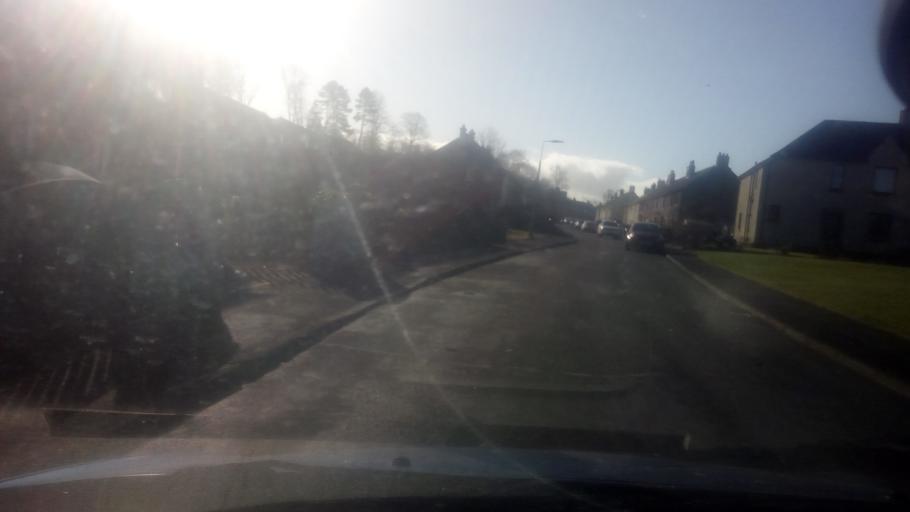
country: GB
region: Scotland
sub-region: The Scottish Borders
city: Jedburgh
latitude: 55.4814
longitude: -2.5458
